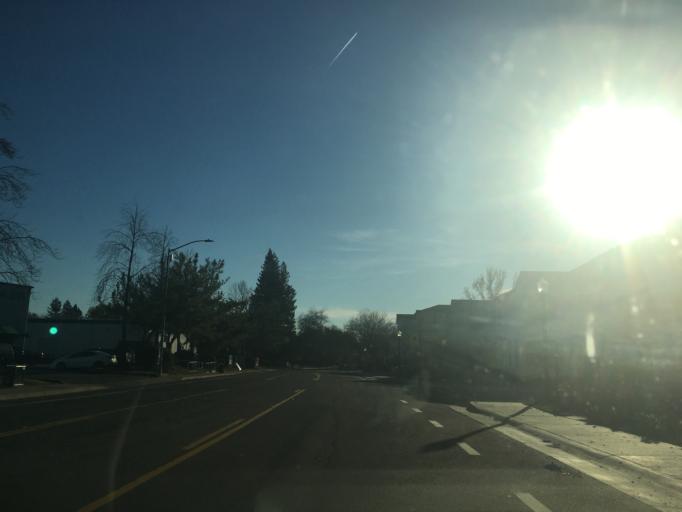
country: US
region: California
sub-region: Sacramento County
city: Sacramento
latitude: 38.5620
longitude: -121.5089
